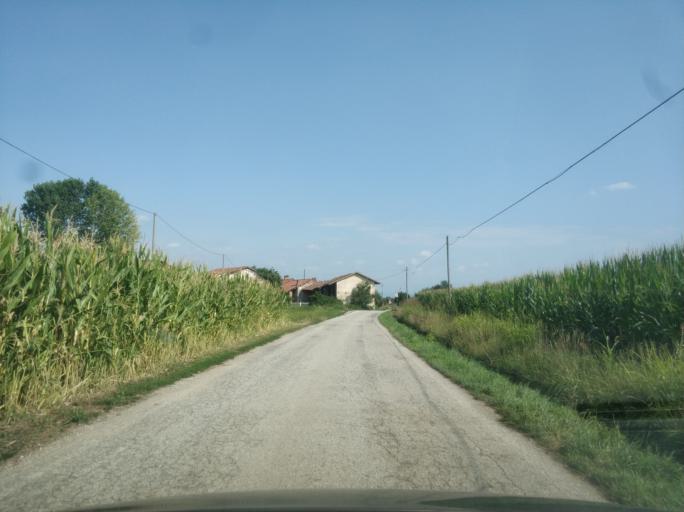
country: IT
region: Piedmont
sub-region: Provincia di Cuneo
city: Roata Rossi
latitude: 44.4535
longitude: 7.4798
